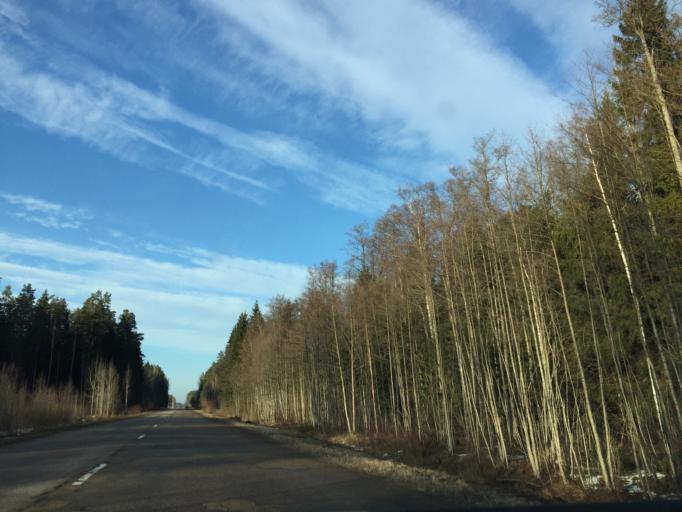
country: LV
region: Lecava
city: Iecava
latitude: 56.7084
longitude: 24.1130
